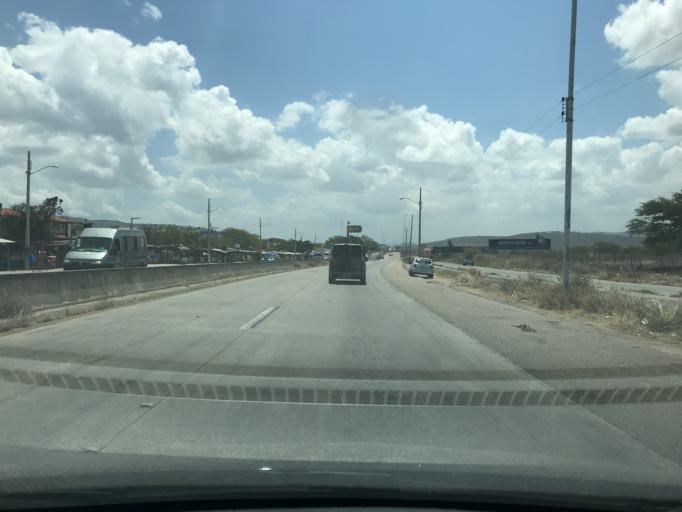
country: BR
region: Pernambuco
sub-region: Bezerros
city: Bezerros
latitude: -8.3005
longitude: -35.8478
